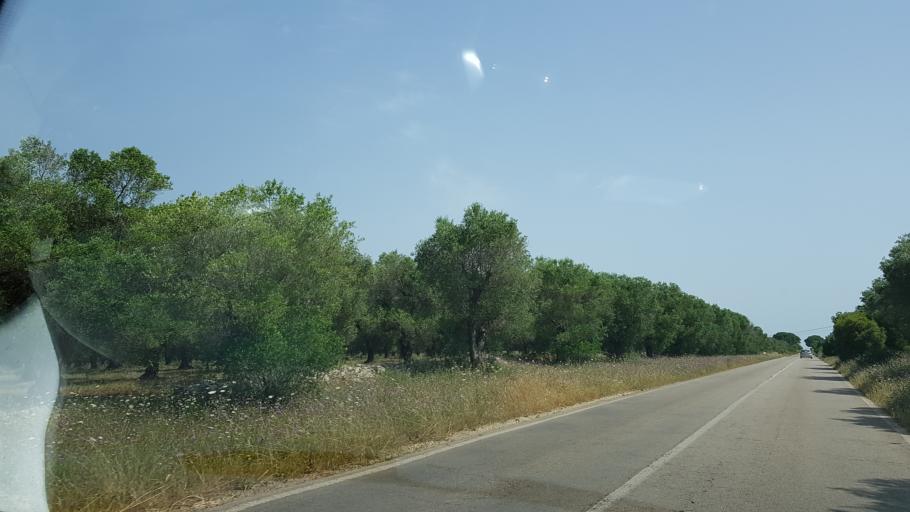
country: IT
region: Apulia
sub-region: Provincia di Brindisi
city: San Pancrazio Salentino
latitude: 40.3494
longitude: 17.8461
